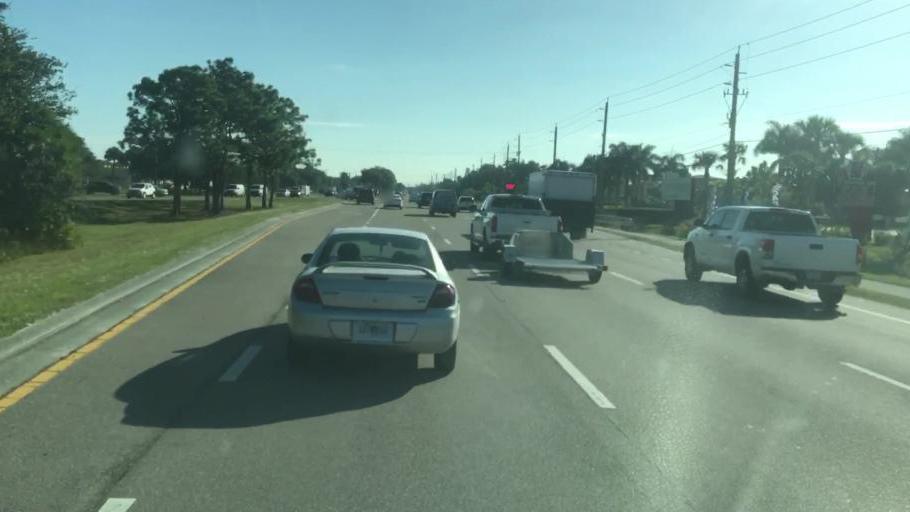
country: US
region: Florida
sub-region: Lee County
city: Villas
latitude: 26.5471
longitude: -81.8097
